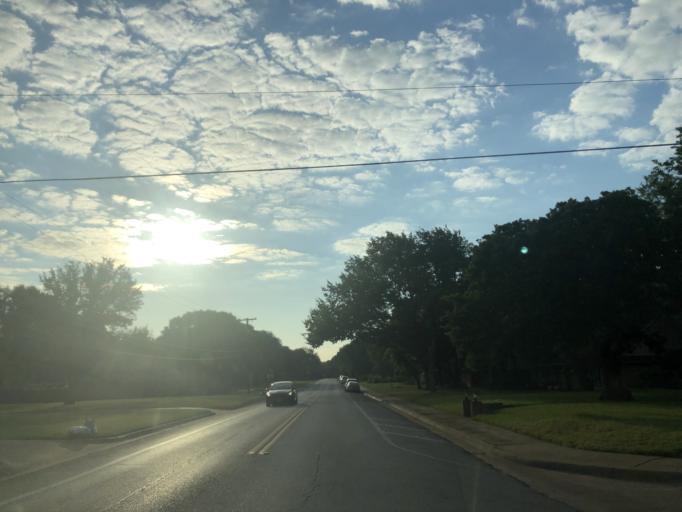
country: US
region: Texas
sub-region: Dallas County
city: Grand Prairie
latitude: 32.7643
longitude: -97.0170
